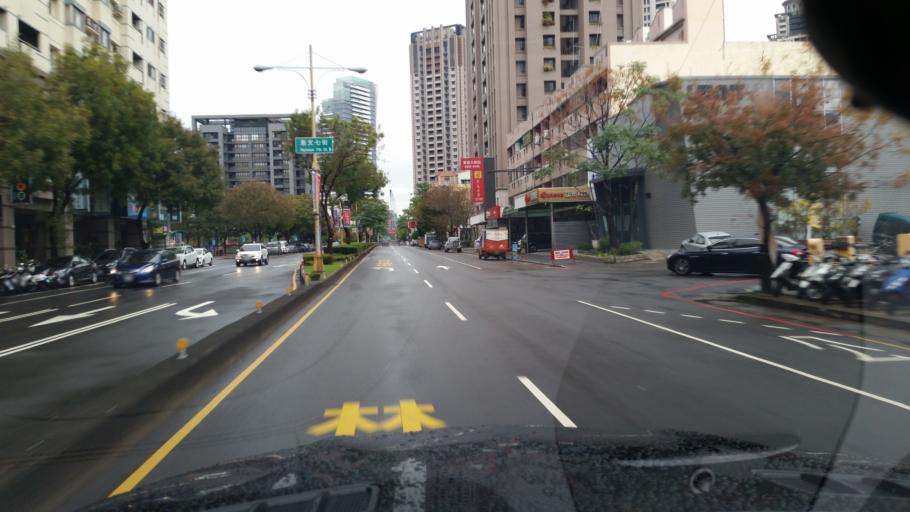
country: TW
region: Taiwan
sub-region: Taichung City
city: Taichung
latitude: 24.1561
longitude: 120.6364
